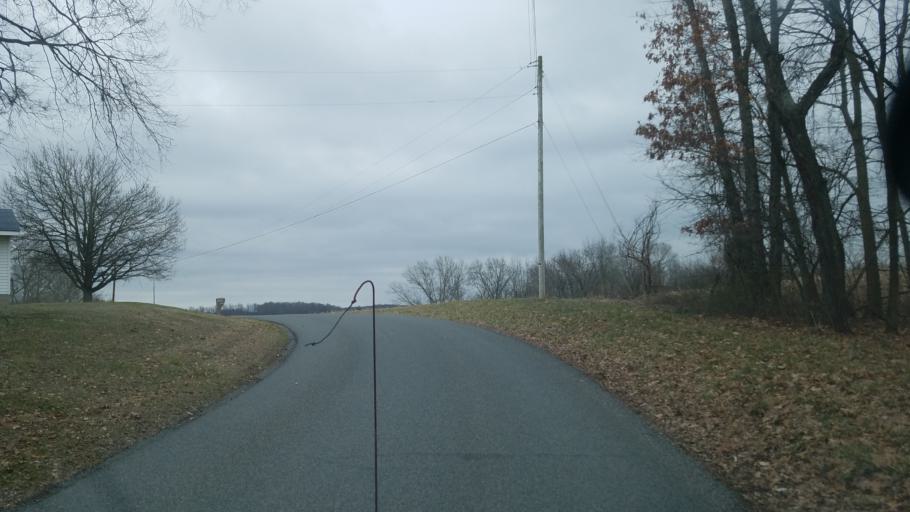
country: US
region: Ohio
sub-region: Licking County
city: Utica
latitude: 40.1986
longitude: -82.4047
